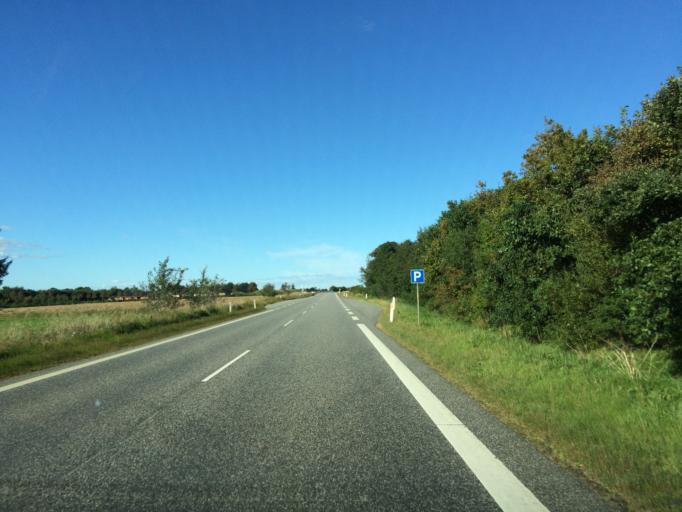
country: DK
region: Central Jutland
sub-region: Holstebro Kommune
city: Holstebro
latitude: 56.3069
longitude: 8.6039
